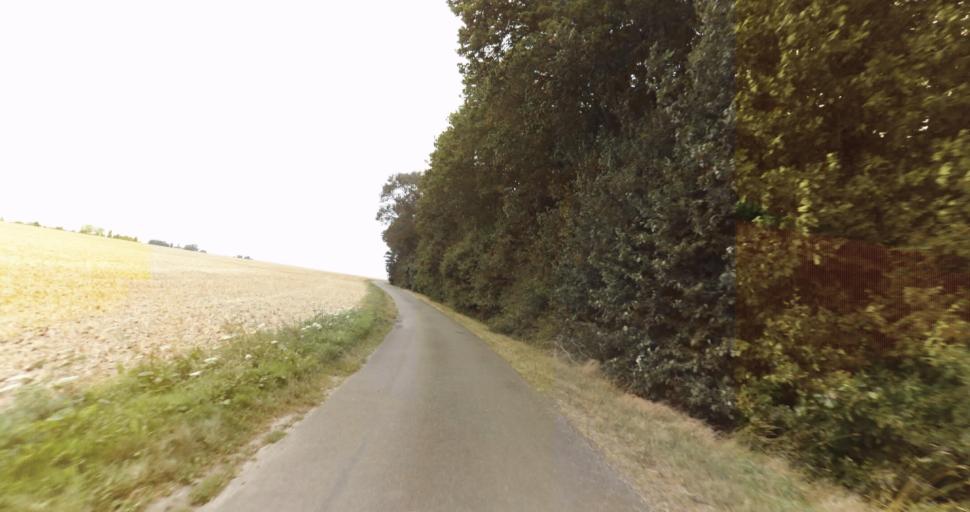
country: FR
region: Haute-Normandie
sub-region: Departement de l'Eure
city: La Couture-Boussey
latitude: 48.9025
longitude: 1.3631
